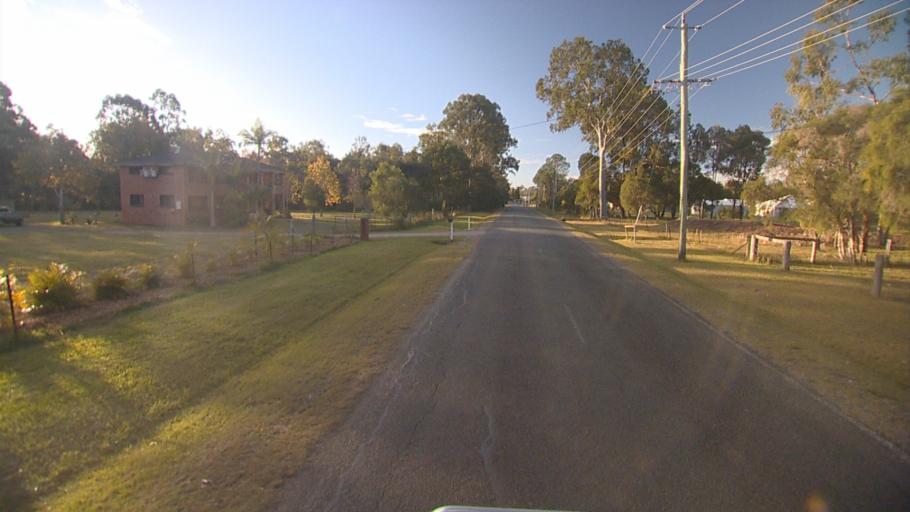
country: AU
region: Queensland
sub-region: Logan
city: Waterford West
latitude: -27.7217
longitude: 153.1420
